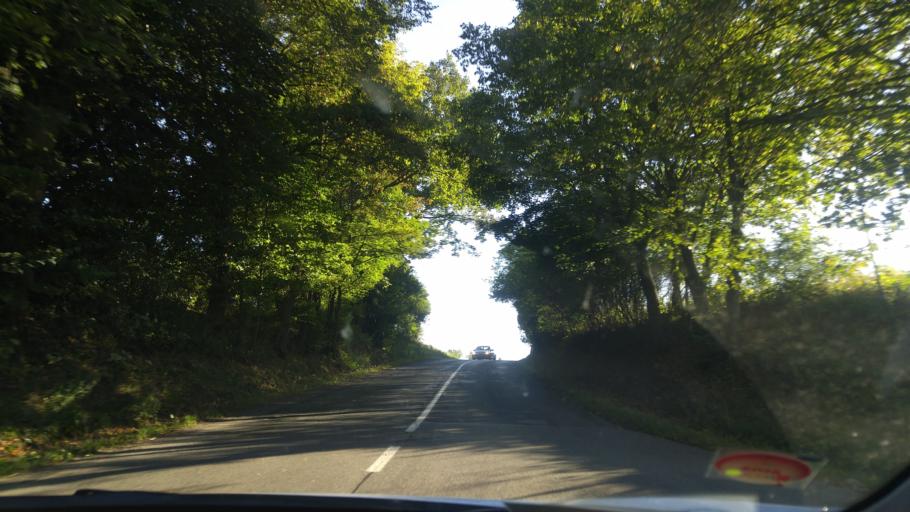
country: CZ
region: South Moravian
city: Veverska Bityska
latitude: 49.2415
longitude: 16.4439
